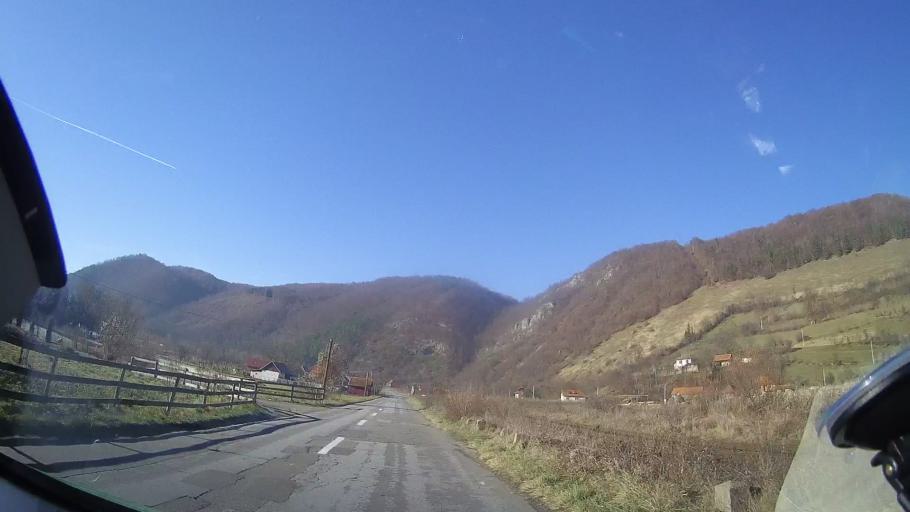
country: RO
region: Bihor
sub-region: Comuna Bulz
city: Bulz
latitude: 46.9487
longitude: 22.6806
